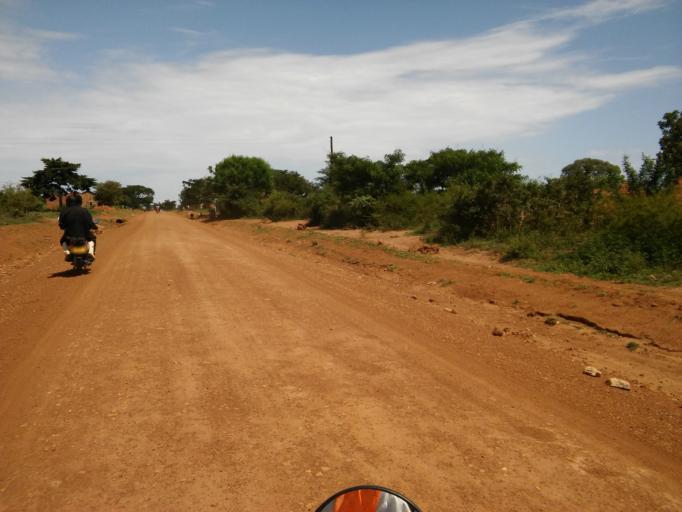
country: UG
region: Eastern Region
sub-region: Kumi District
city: Kumi
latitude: 1.4792
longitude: 33.8906
